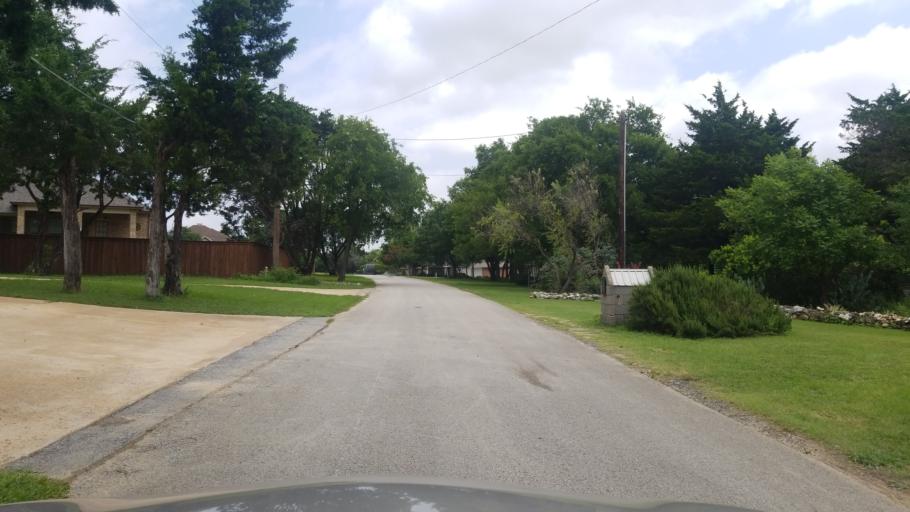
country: US
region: Texas
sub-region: Dallas County
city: Duncanville
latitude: 32.6827
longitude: -96.9310
